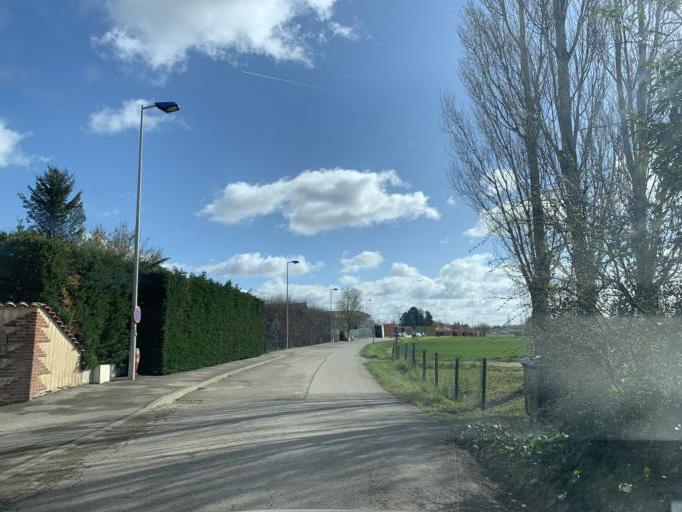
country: FR
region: Rhone-Alpes
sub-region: Departement de l'Ain
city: Saint-Andre-de-Corcy
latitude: 45.9509
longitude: 4.9793
